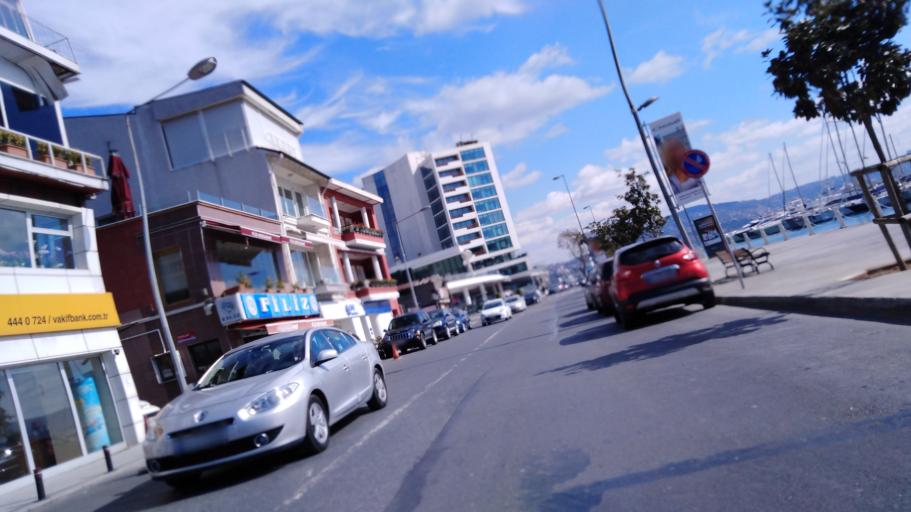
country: TR
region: Istanbul
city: Sisli
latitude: 41.1393
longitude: 29.0552
